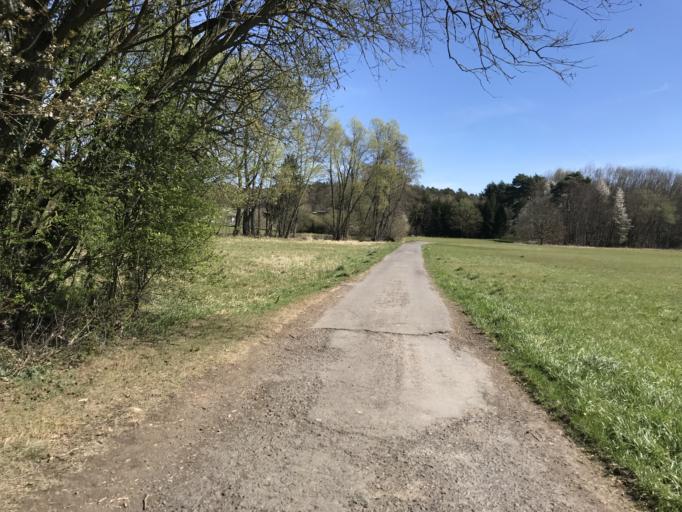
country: DE
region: Hesse
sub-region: Regierungsbezirk Giessen
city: Alten Buseck
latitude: 50.6417
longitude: 8.7427
